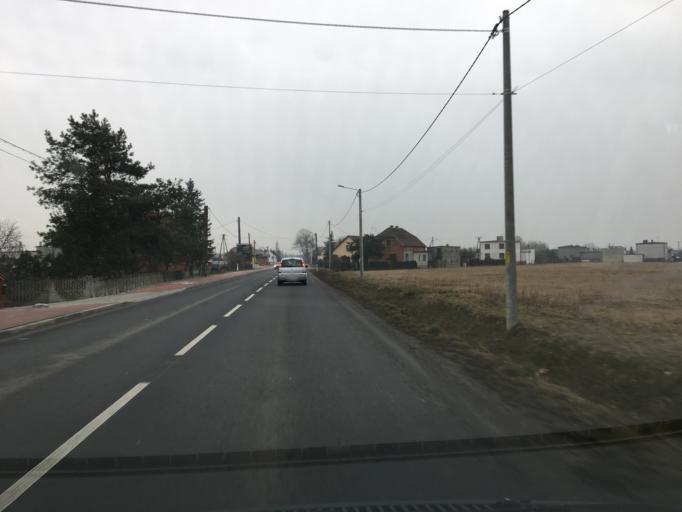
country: PL
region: Opole Voivodeship
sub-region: Powiat kedzierzynsko-kozielski
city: Kedzierzyn-Kozle
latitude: 50.3175
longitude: 18.2241
